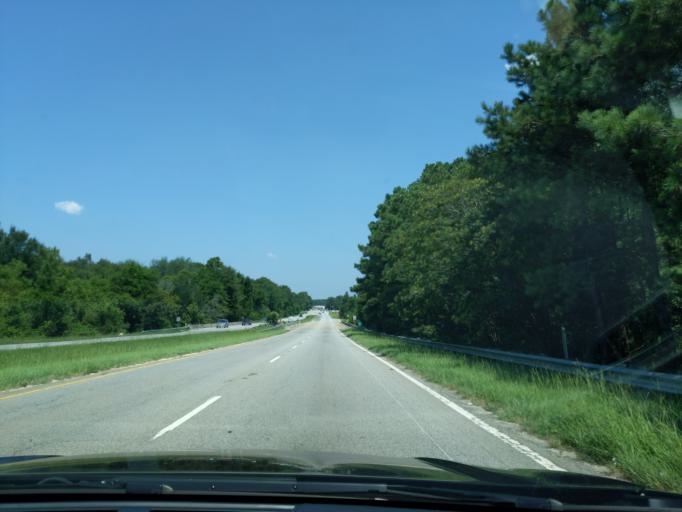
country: US
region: South Carolina
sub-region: Richland County
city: Forest Acres
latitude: 33.9542
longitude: -80.9796
